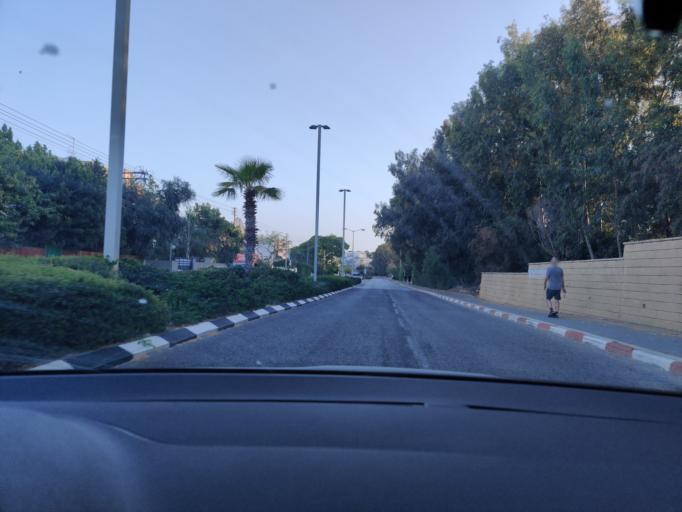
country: IL
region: Haifa
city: Hadera
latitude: 32.4774
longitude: 34.9532
